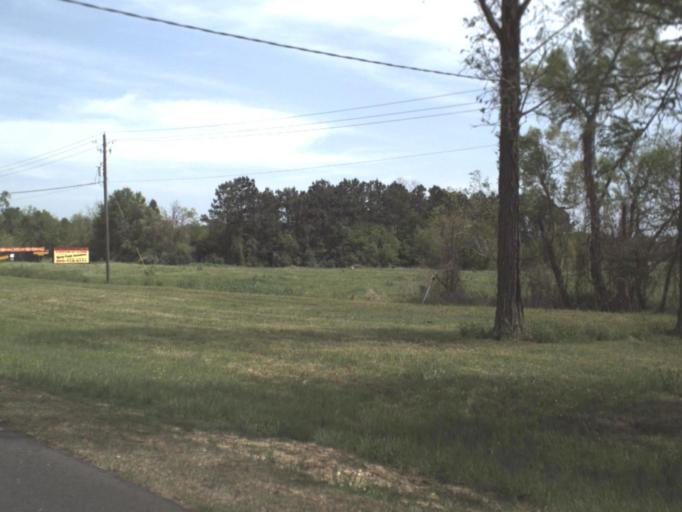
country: US
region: Florida
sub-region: Escambia County
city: Ensley
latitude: 30.5340
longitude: -87.2998
